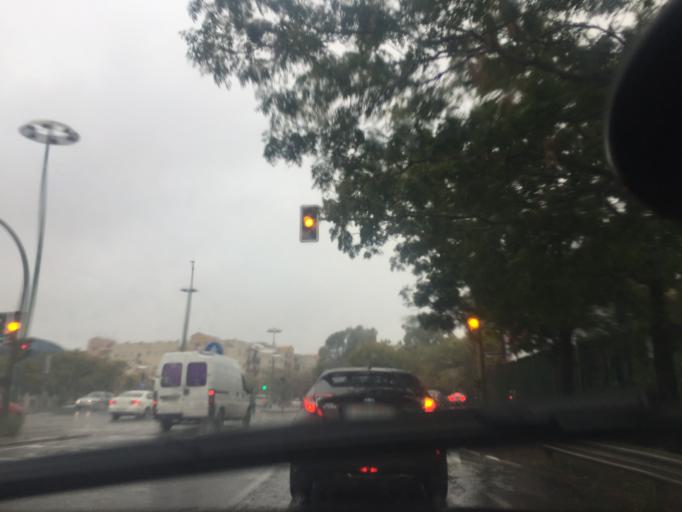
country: ES
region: Andalusia
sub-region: Provincia de Sevilla
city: Sevilla
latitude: 37.3610
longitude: -5.9583
